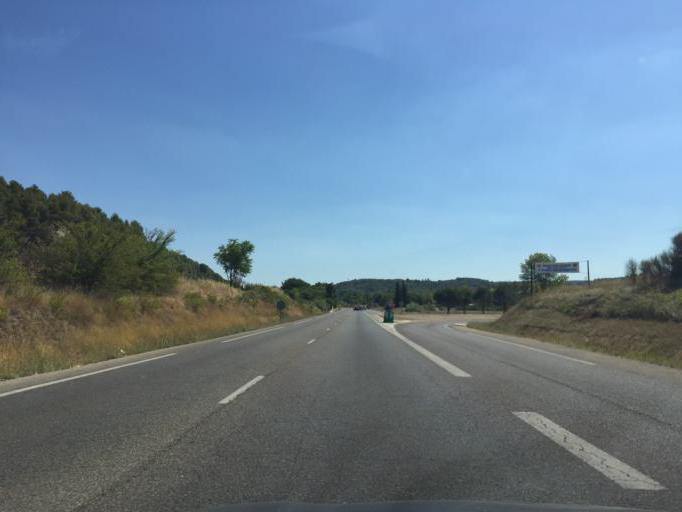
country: FR
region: Provence-Alpes-Cote d'Azur
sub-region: Departement du Vaucluse
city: Menerbes
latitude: 43.8583
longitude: 5.1991
